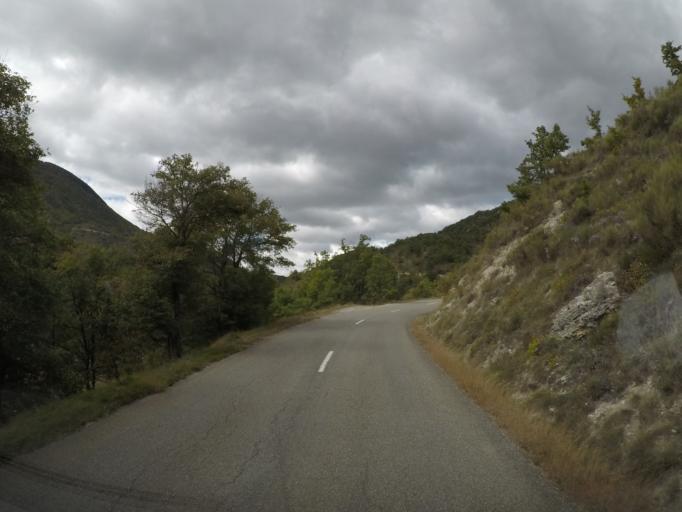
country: FR
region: Provence-Alpes-Cote d'Azur
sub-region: Departement du Vaucluse
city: Sault
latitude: 44.1776
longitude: 5.5833
